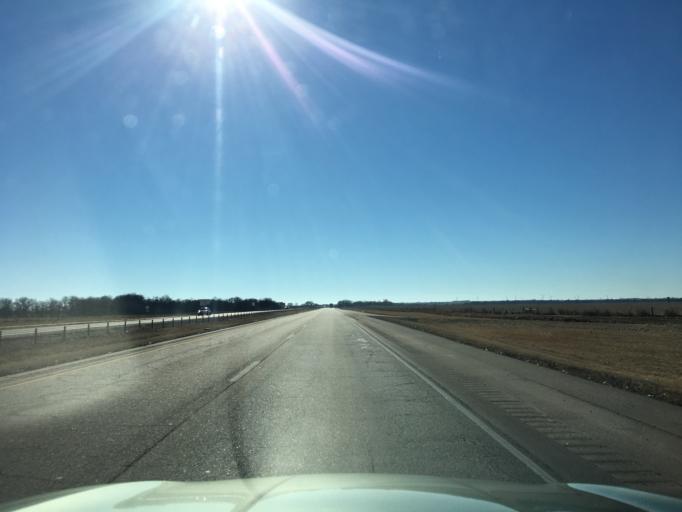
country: US
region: Oklahoma
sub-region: Kay County
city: Blackwell
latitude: 36.9266
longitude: -97.3494
